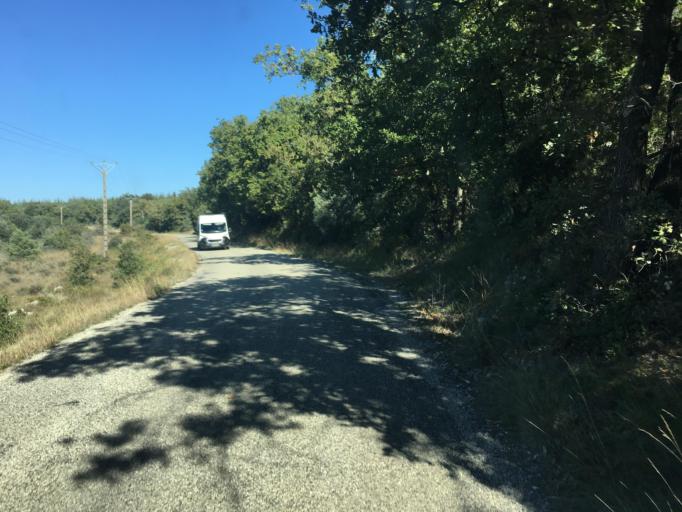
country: FR
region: Languedoc-Roussillon
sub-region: Departement du Gard
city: Montaren-et-Saint-Mediers
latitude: 44.1306
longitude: 4.3116
